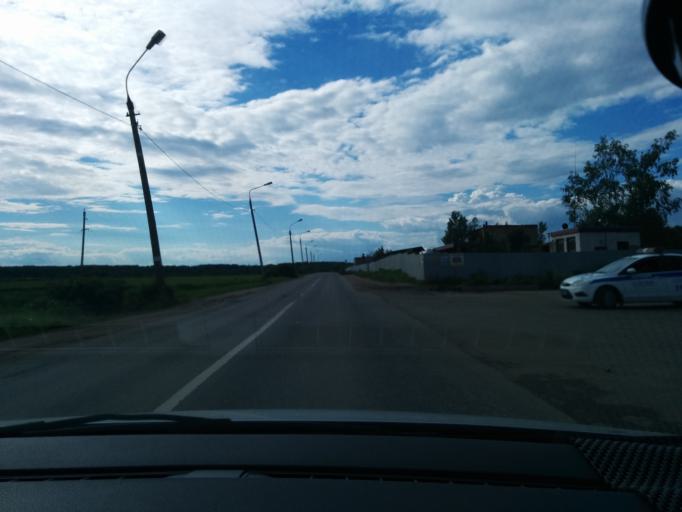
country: RU
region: Moskovskaya
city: Lugovaya
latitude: 56.0431
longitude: 37.4771
